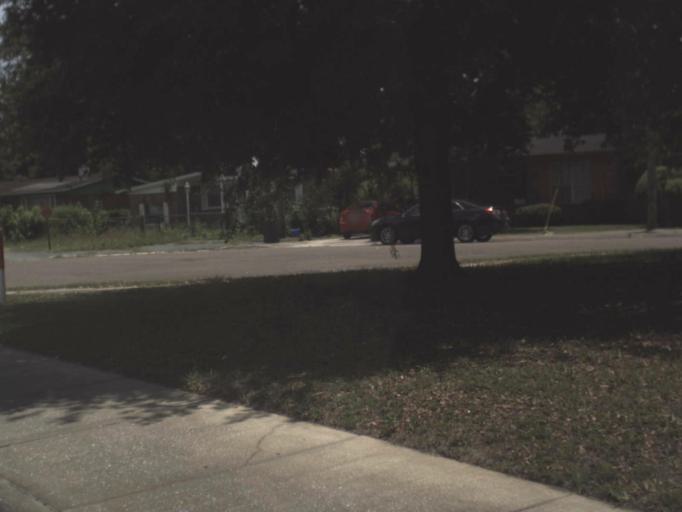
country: US
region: Florida
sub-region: Duval County
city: Jacksonville
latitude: 30.3495
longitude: -81.6982
